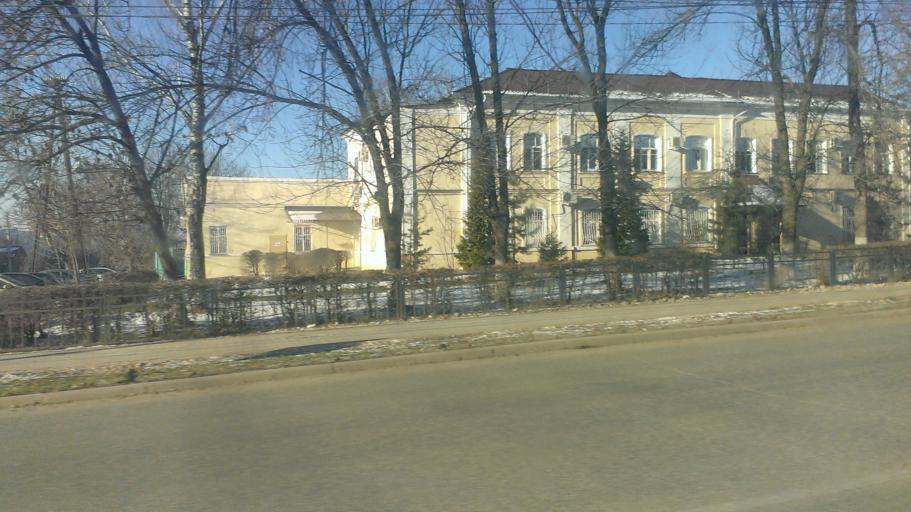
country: RU
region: Tula
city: Tula
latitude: 54.2051
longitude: 37.6530
